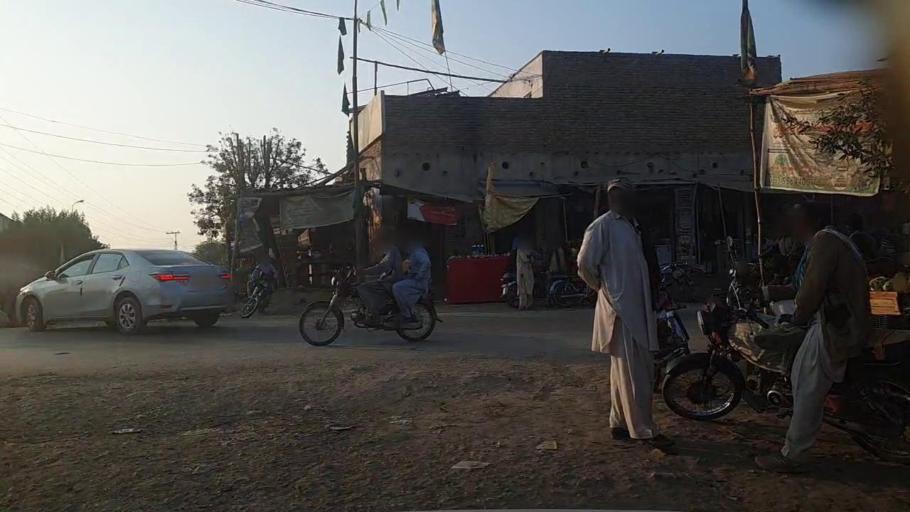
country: PK
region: Sindh
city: Darya Khan Marri
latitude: 26.6866
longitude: 68.3125
